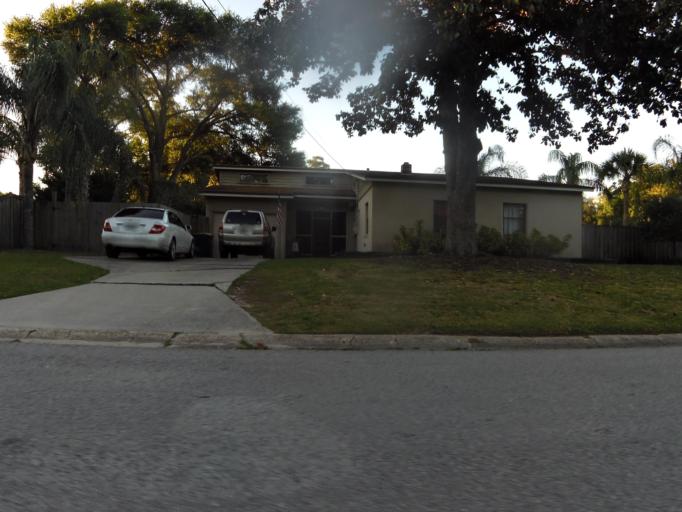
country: US
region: Florida
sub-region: Duval County
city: Jacksonville
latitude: 30.2588
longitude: -81.6390
